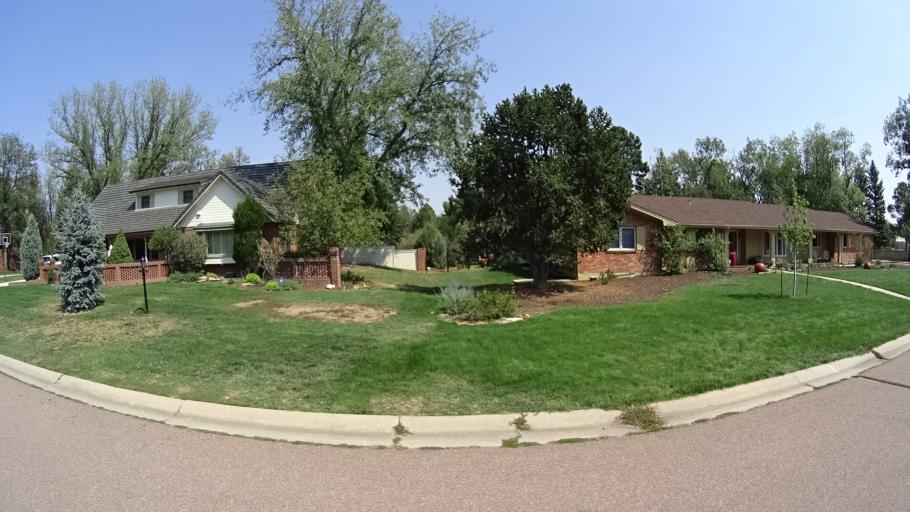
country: US
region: Colorado
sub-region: El Paso County
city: Colorado Springs
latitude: 38.7913
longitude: -104.8427
